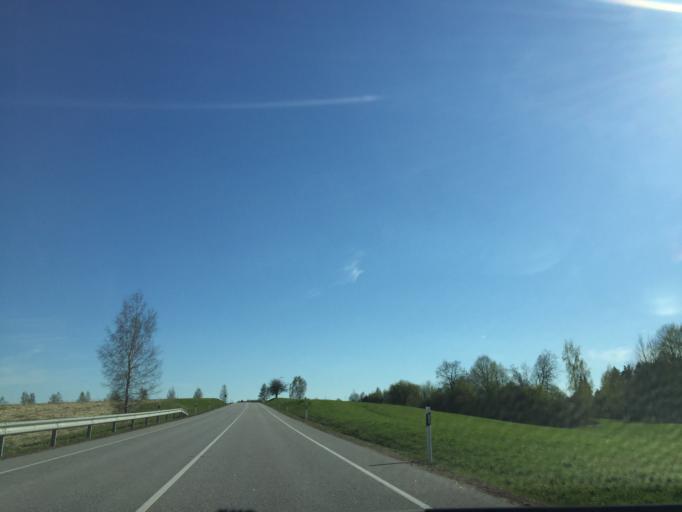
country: EE
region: Vorumaa
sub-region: Antsla vald
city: Vana-Antsla
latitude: 57.8835
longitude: 26.2829
